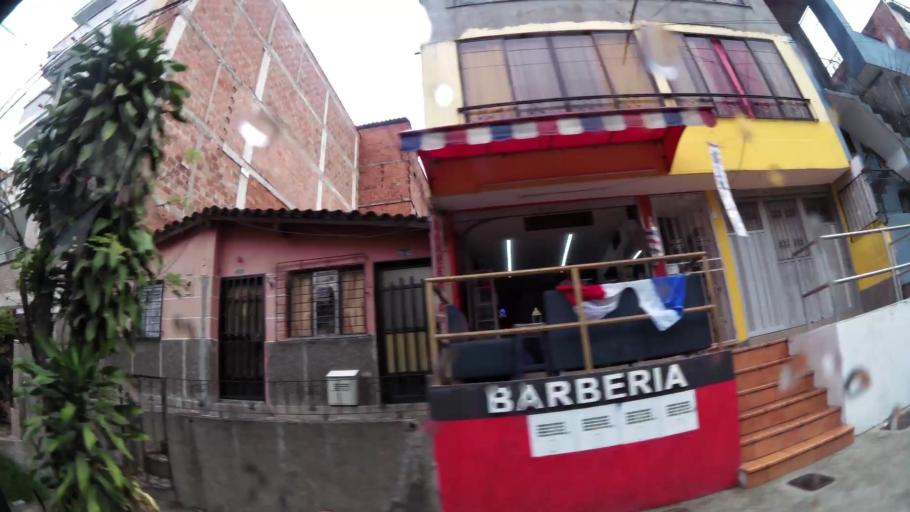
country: CO
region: Antioquia
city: Itagui
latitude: 6.1883
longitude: -75.5944
